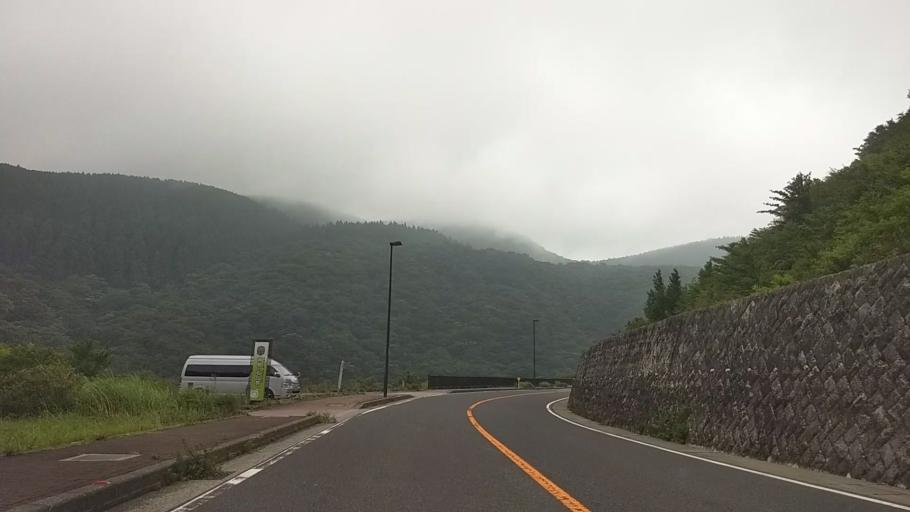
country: JP
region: Kanagawa
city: Hakone
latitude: 35.2123
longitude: 139.0362
